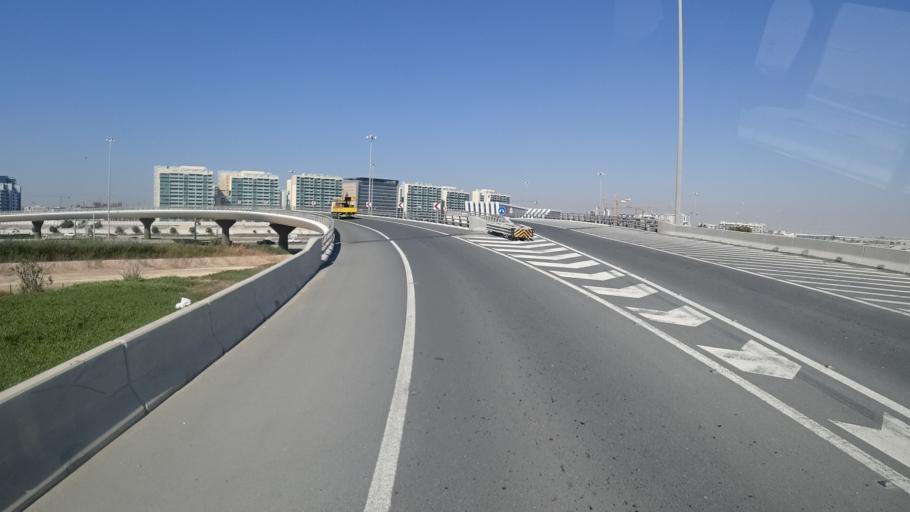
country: AE
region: Abu Dhabi
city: Abu Dhabi
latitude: 24.4442
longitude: 54.6035
